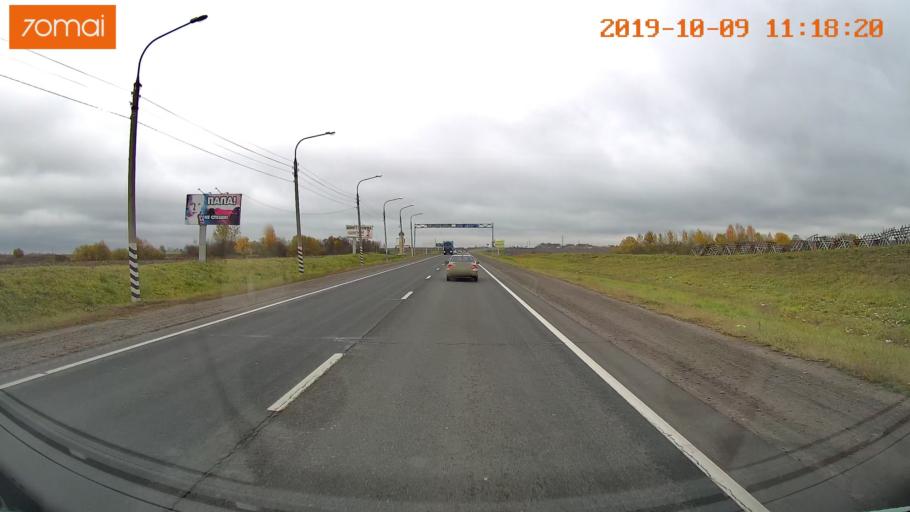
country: RU
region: Vologda
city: Vologda
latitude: 59.1686
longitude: 39.9132
